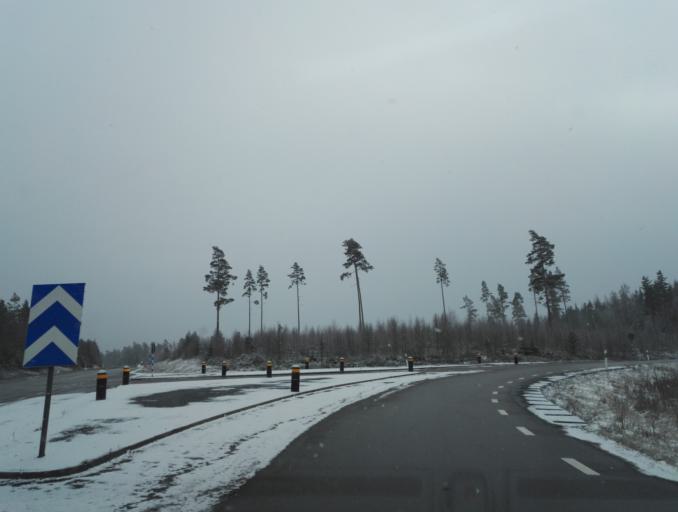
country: SE
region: Kronoberg
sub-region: Uppvidinge Kommun
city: Lenhovda
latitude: 56.9215
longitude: 15.3648
